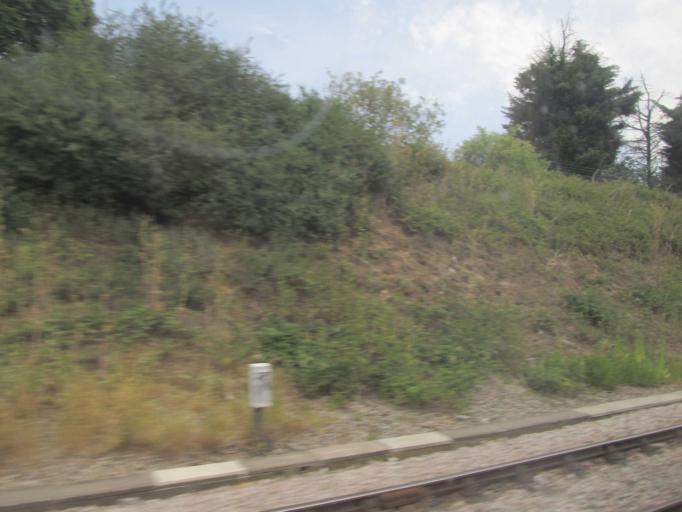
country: GB
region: England
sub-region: Buckinghamshire
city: Iver
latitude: 51.5092
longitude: -0.5030
